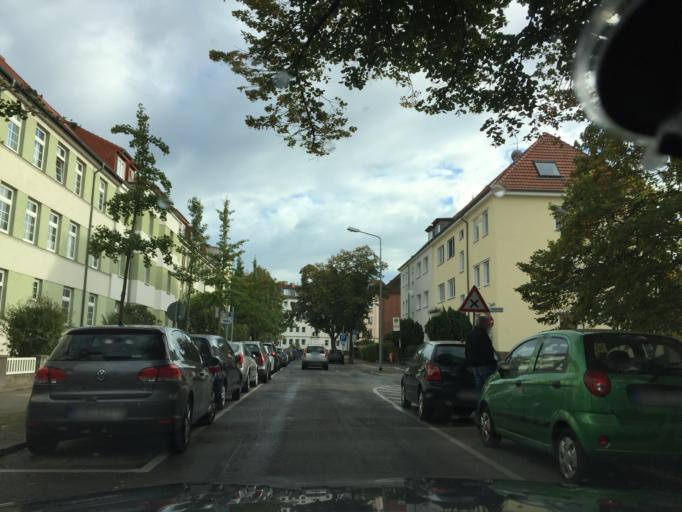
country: DE
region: Mecklenburg-Vorpommern
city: Warnemuende
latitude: 54.1741
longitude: 12.0854
